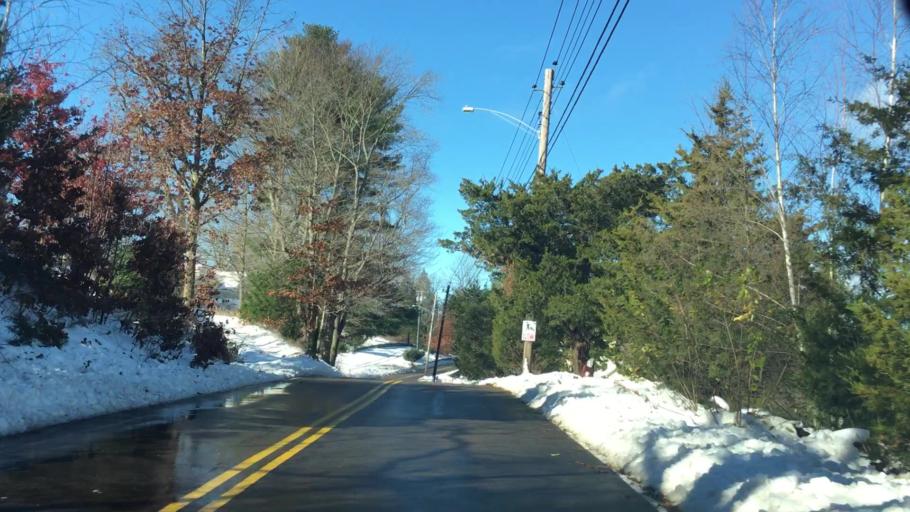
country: US
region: Connecticut
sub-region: Fairfield County
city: Shelton
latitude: 41.3325
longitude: -73.1698
